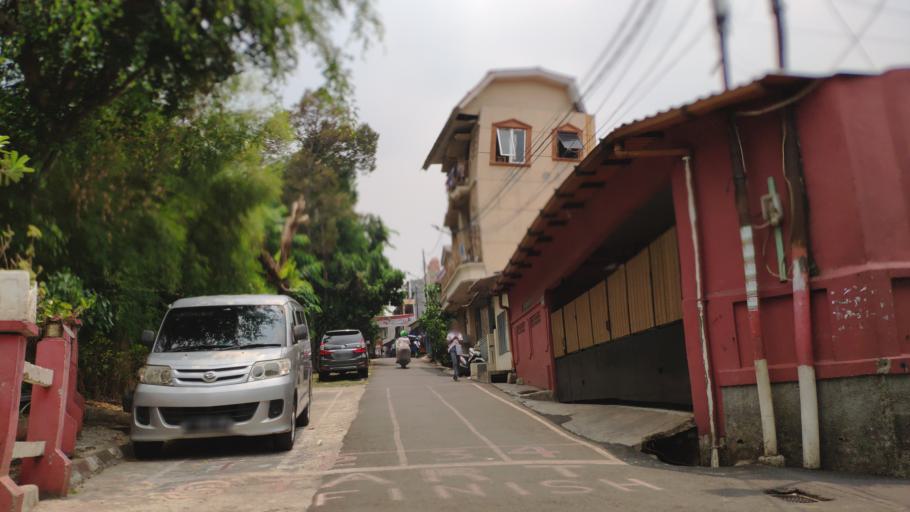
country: ID
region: Banten
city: South Tangerang
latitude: -6.2598
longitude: 106.7732
